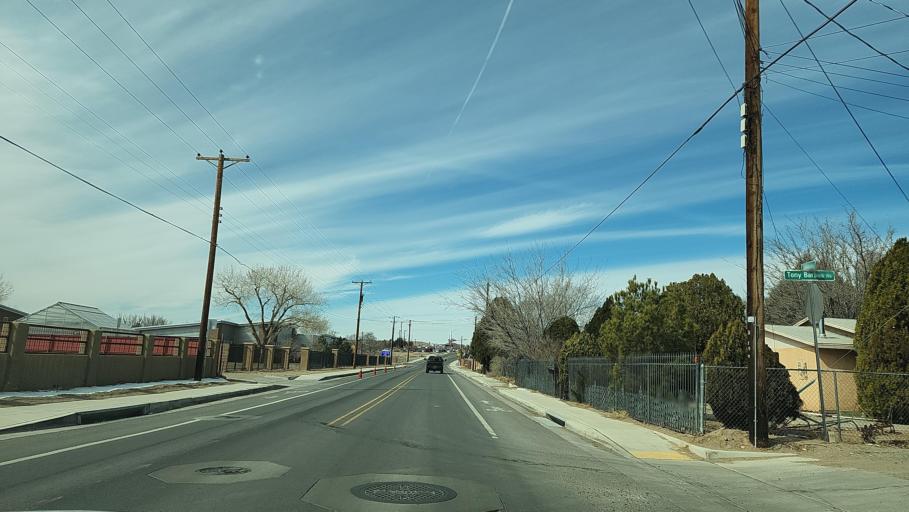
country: US
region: New Mexico
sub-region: Bernalillo County
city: South Valley
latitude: 35.0362
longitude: -106.7086
